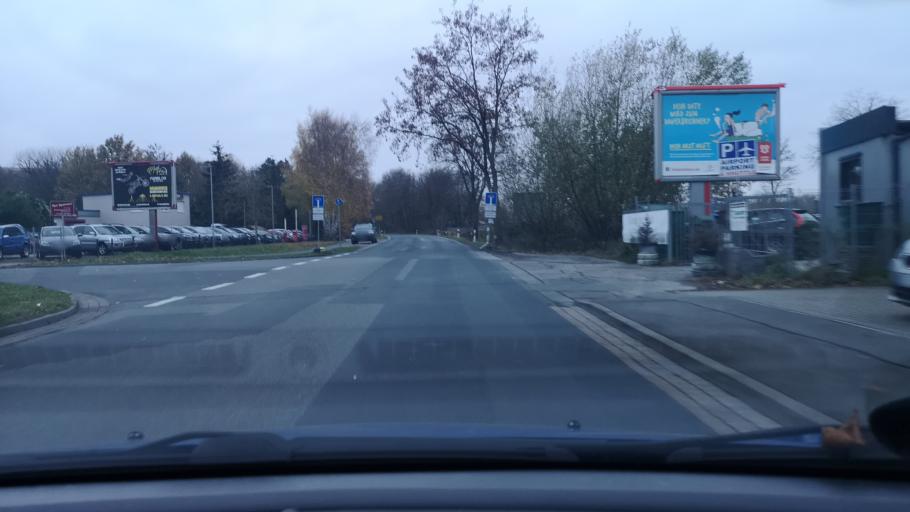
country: DE
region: Lower Saxony
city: Langenhagen
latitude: 52.4529
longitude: 9.7235
